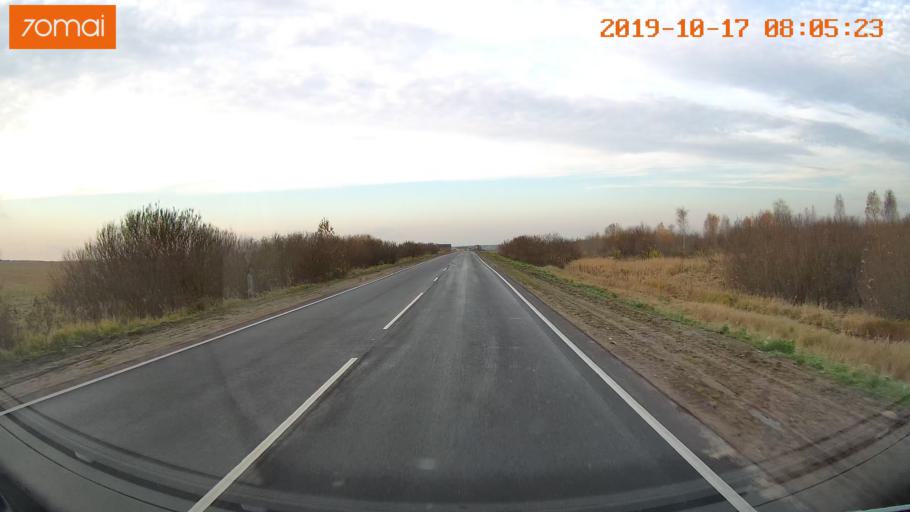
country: RU
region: Vladimir
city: Kol'chugino
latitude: 56.3352
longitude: 39.4167
